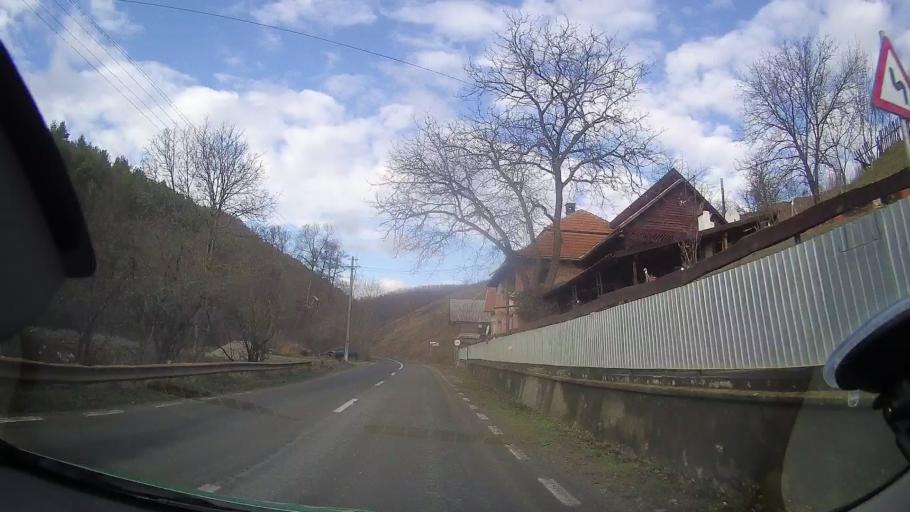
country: RO
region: Cluj
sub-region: Comuna Baisoara
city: Baisoara
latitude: 46.5828
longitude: 23.4546
